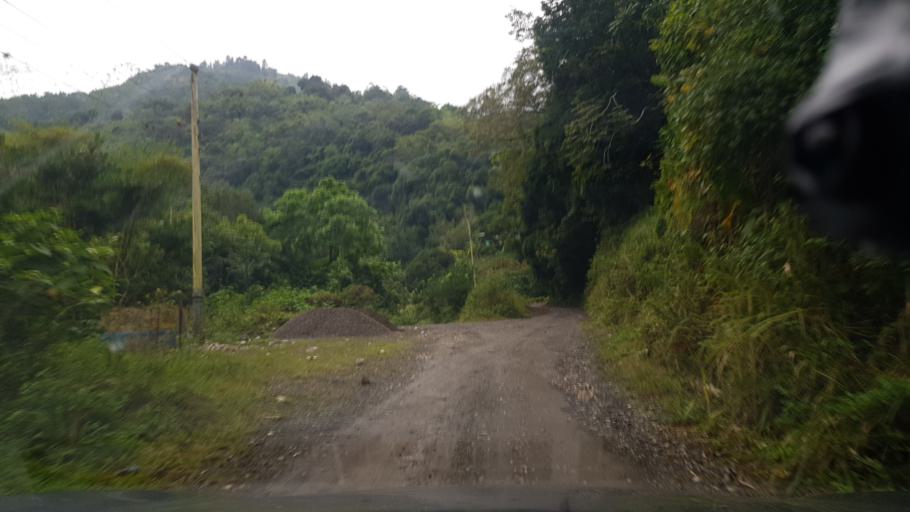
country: JM
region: Saint Andrew
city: Stony Hill
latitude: 18.1163
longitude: -76.7174
